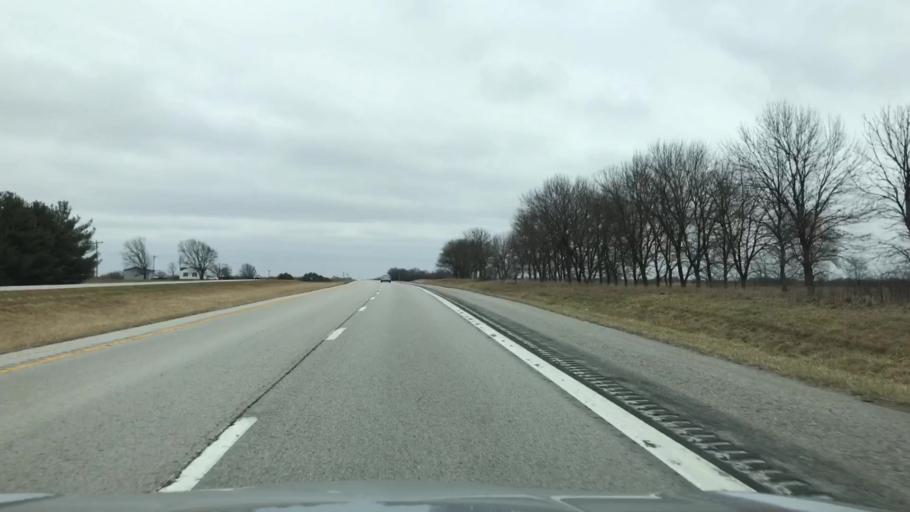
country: US
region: Missouri
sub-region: Livingston County
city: Chillicothe
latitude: 39.7771
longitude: -93.3802
